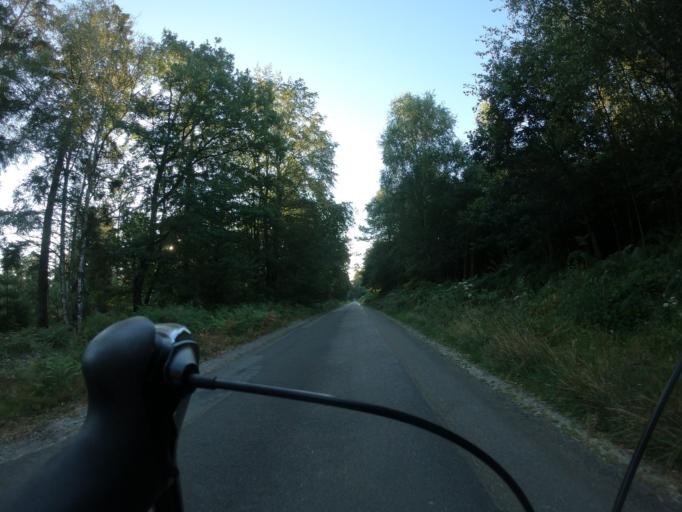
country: FR
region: Lower Normandy
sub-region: Departement de l'Orne
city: Magny-le-Desert
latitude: 48.5421
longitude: -0.3422
